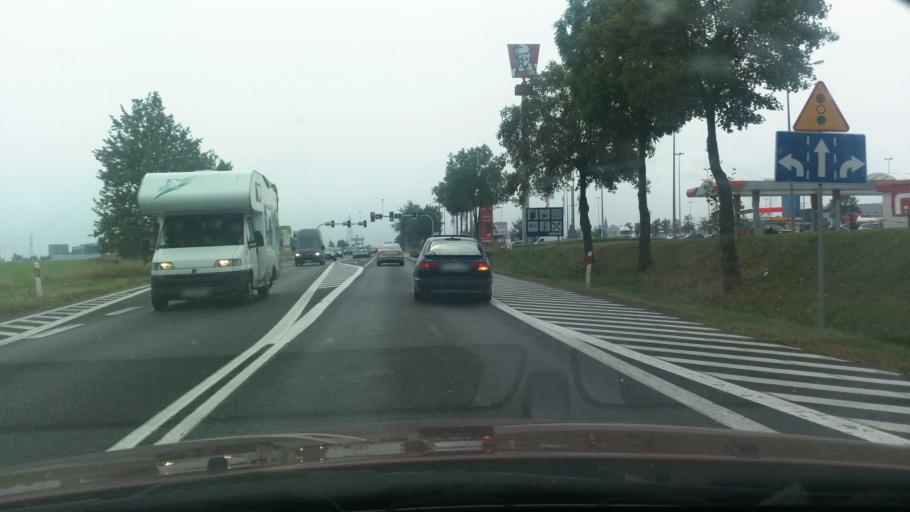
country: PL
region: Lower Silesian Voivodeship
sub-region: Powiat zgorzelecki
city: Lagow
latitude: 51.1612
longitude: 15.0294
